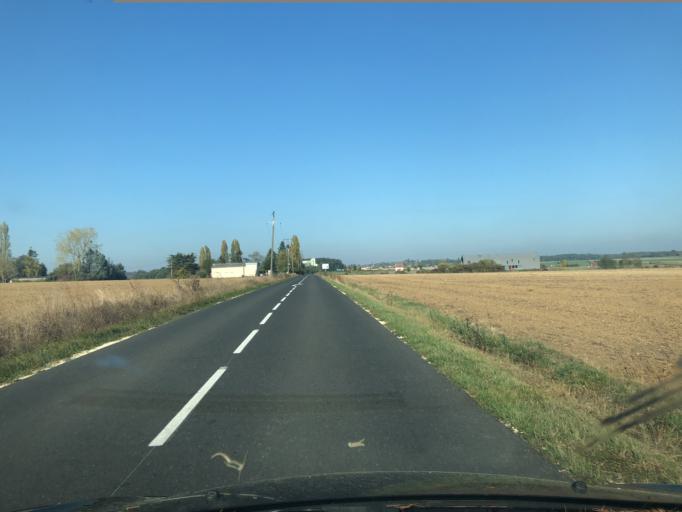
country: FR
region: Centre
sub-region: Departement d'Indre-et-Loire
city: Rouziers-de-Touraine
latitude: 47.4997
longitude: 0.6529
